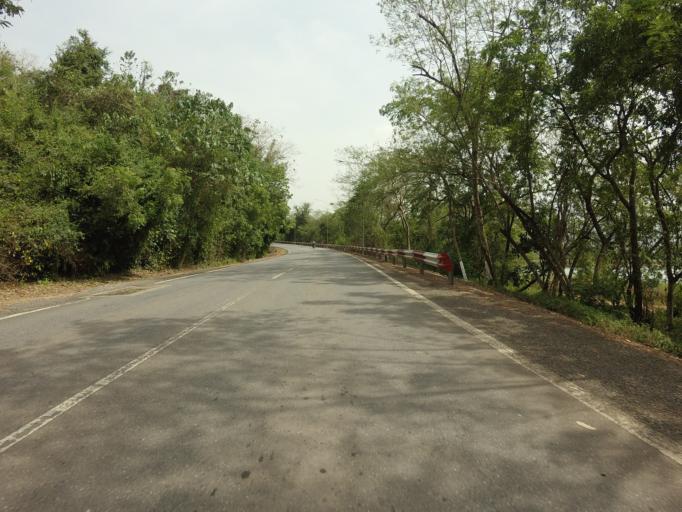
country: GH
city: Akropong
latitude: 6.2809
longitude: 0.0539
